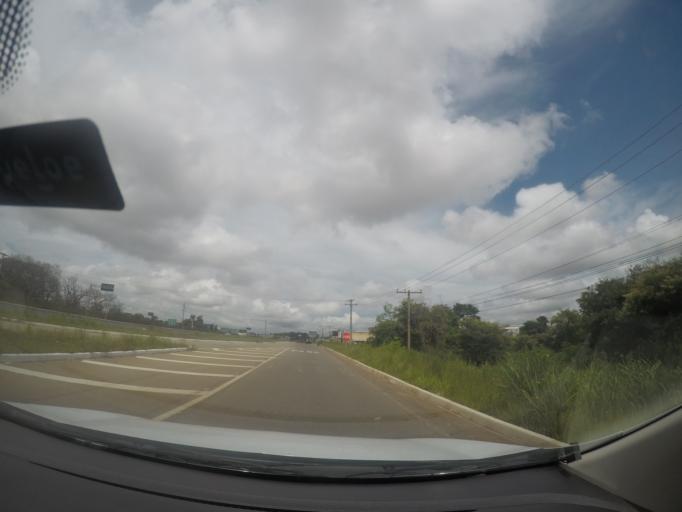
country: BR
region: Goias
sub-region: Goiania
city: Goiania
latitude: -16.7021
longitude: -49.3382
